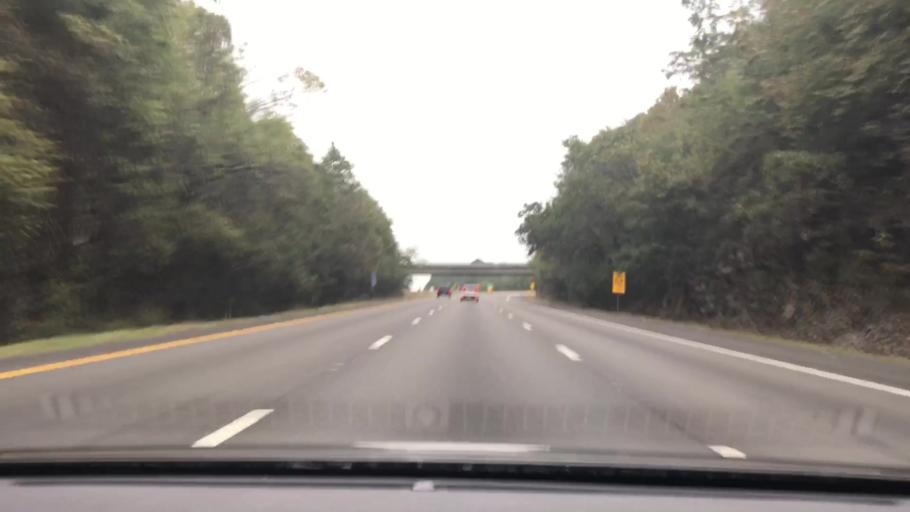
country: US
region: Tennessee
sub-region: Sumner County
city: Millersville
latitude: 36.4158
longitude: -86.7187
